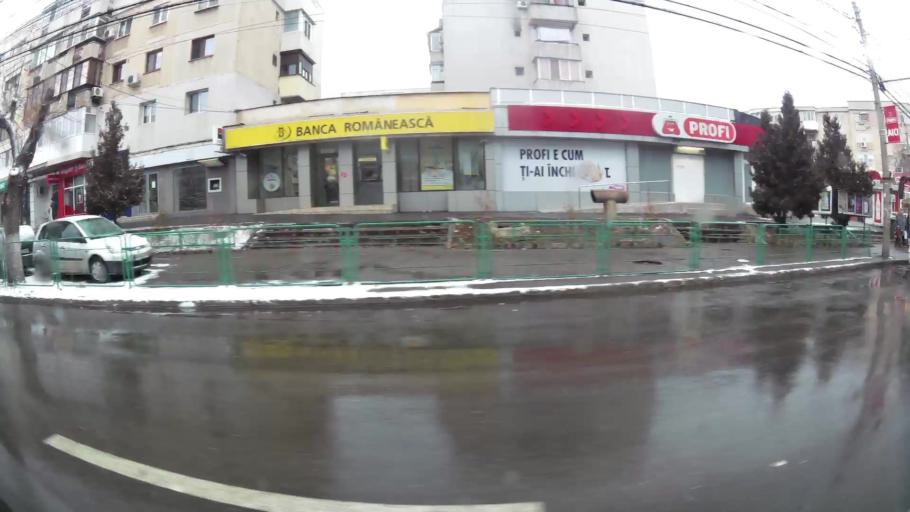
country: RO
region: Prahova
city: Ploiesti
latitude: 44.9379
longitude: 25.9962
